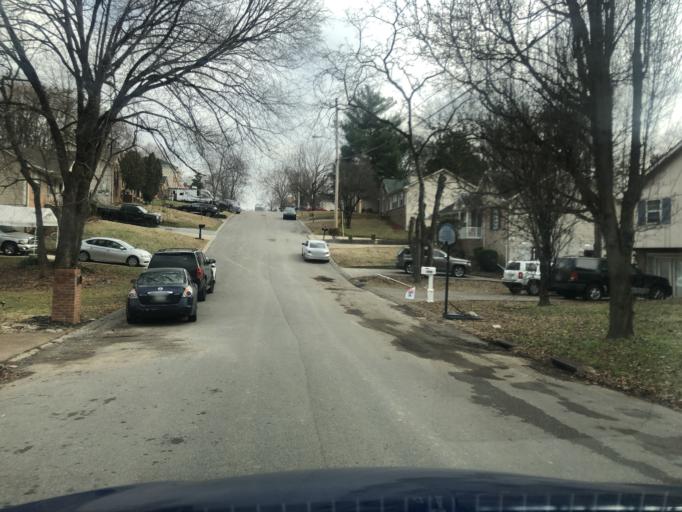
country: US
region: Tennessee
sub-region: Davidson County
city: Oak Hill
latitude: 36.0884
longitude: -86.7106
